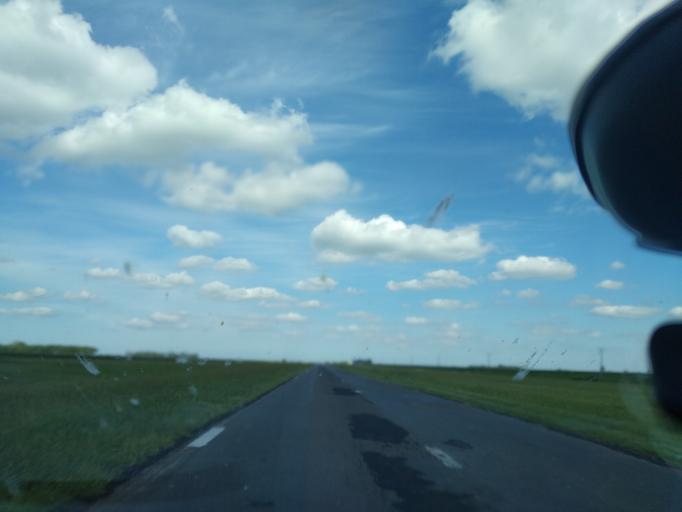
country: AR
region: Santa Fe
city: Carcarana
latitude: -32.8914
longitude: -61.0869
